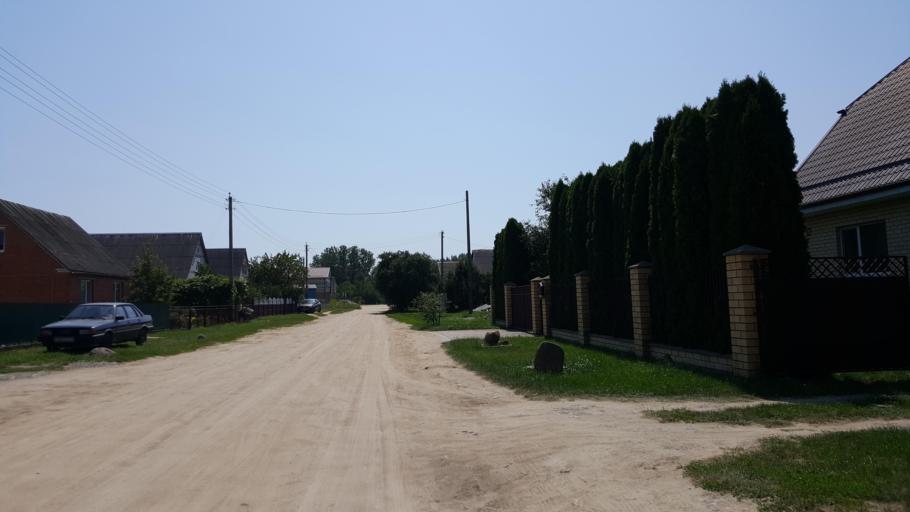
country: BY
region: Brest
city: Zhabinka
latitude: 52.1952
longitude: 23.9771
